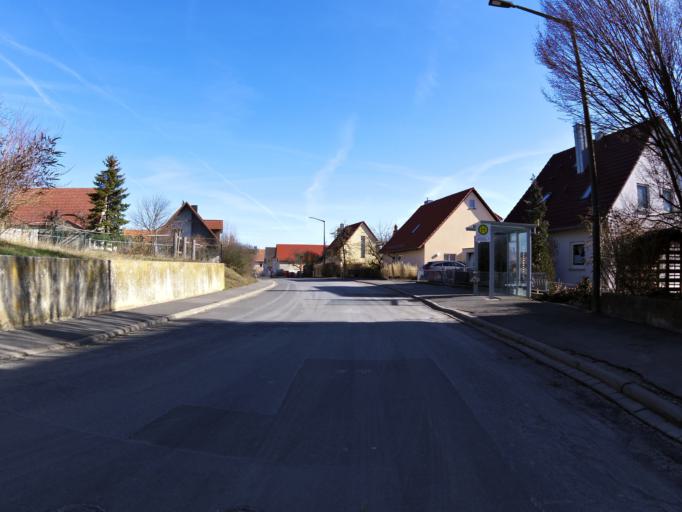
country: DE
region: Bavaria
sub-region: Regierungsbezirk Unterfranken
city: Kurnach
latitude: 49.8585
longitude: 10.0084
